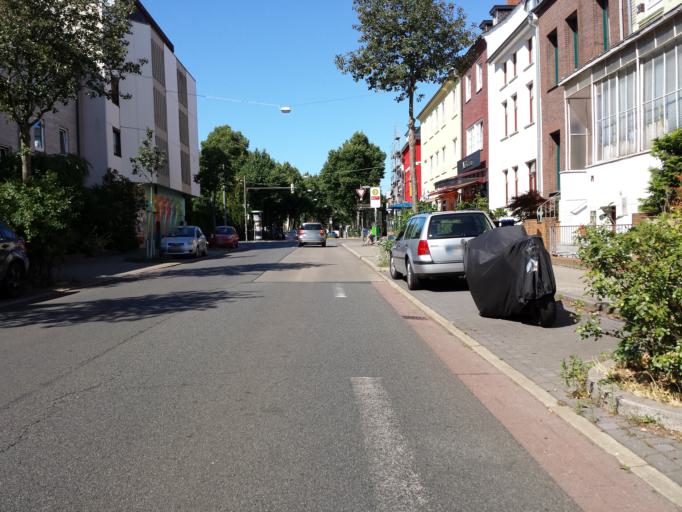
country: DE
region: Bremen
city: Bremen
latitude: 53.0706
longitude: 8.8503
